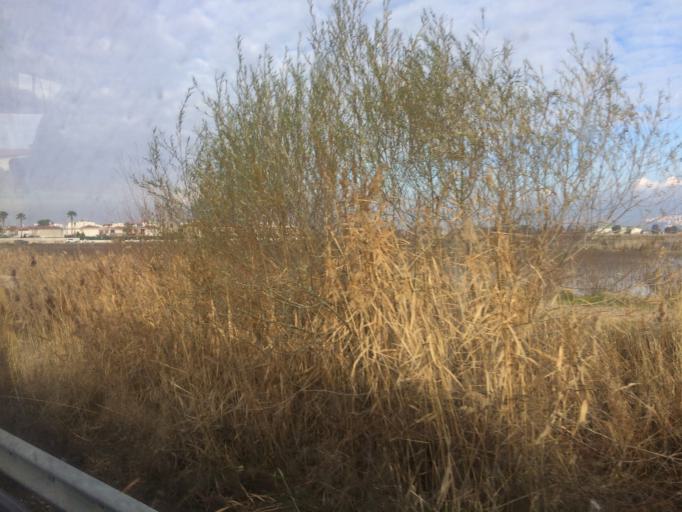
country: TR
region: Izmir
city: Menemen
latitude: 38.4995
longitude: 26.9601
